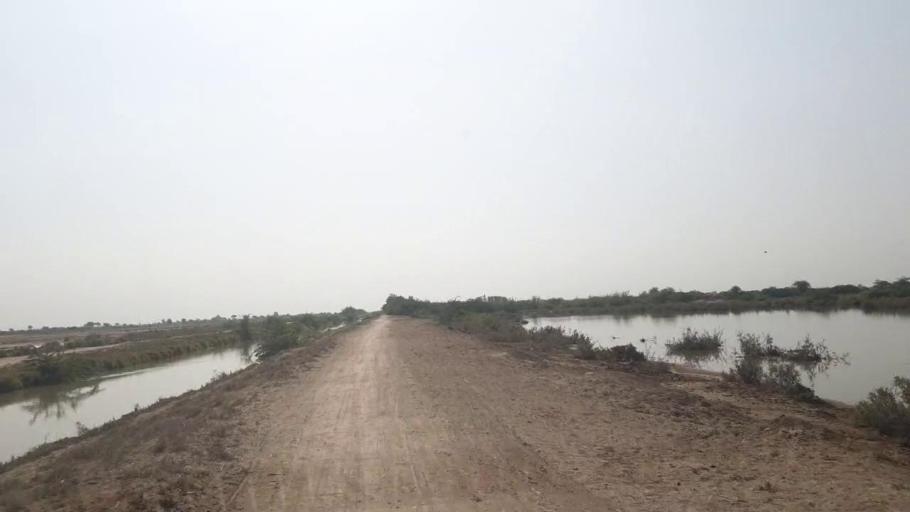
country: PK
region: Sindh
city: Kadhan
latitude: 24.5096
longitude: 68.8503
